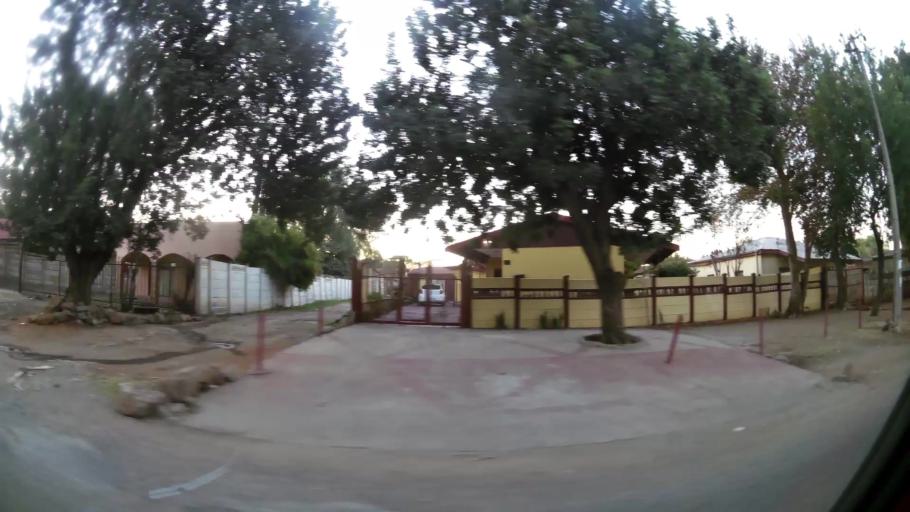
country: ZA
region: North-West
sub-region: Bojanala Platinum District Municipality
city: Rustenburg
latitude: -25.6571
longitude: 27.2380
